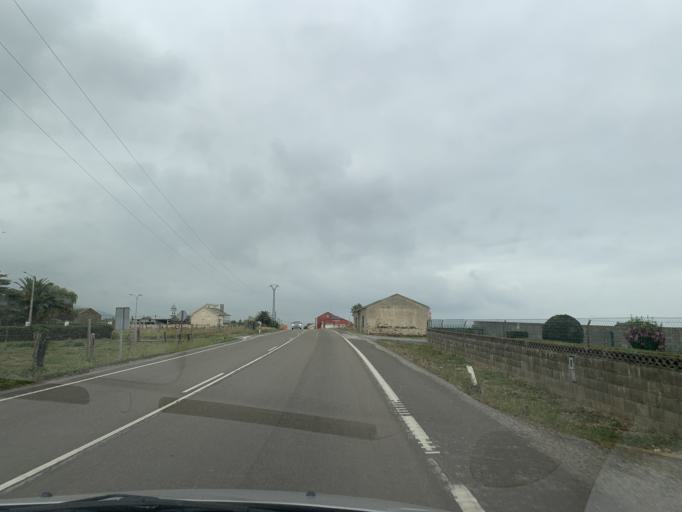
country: ES
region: Galicia
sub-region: Provincia de Lugo
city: Ribadeo
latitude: 43.5454
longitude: -7.0875
